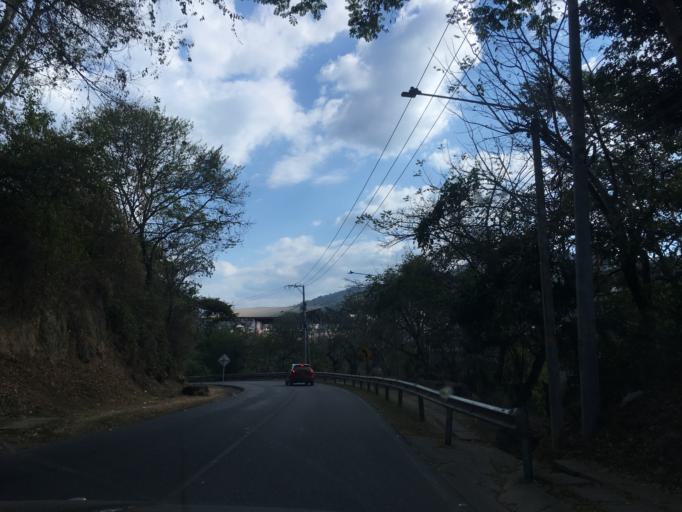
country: CO
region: Santander
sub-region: San Gil
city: San Gil
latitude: 6.5625
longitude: -73.1414
